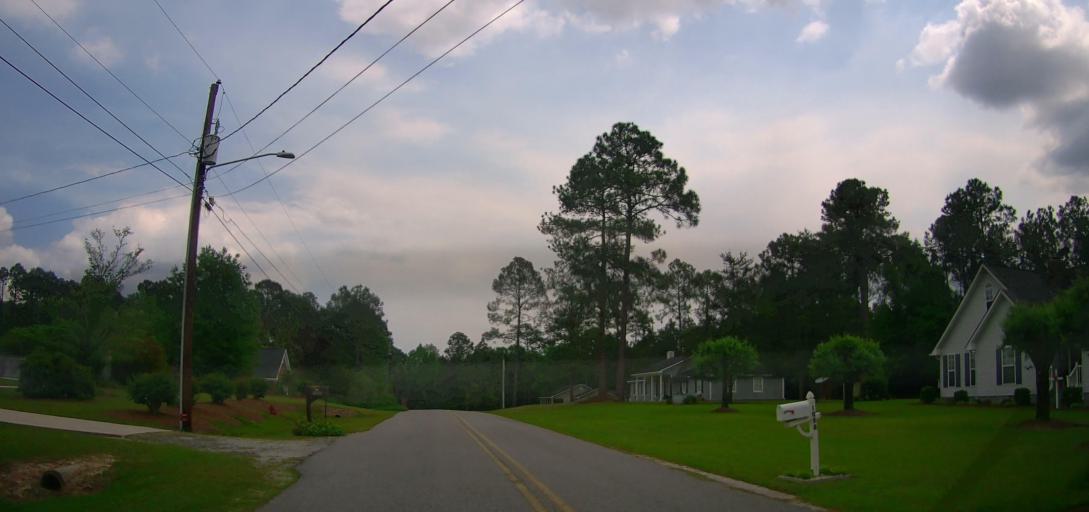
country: US
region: Georgia
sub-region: Treutlen County
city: Soperton
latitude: 32.3641
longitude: -82.5885
